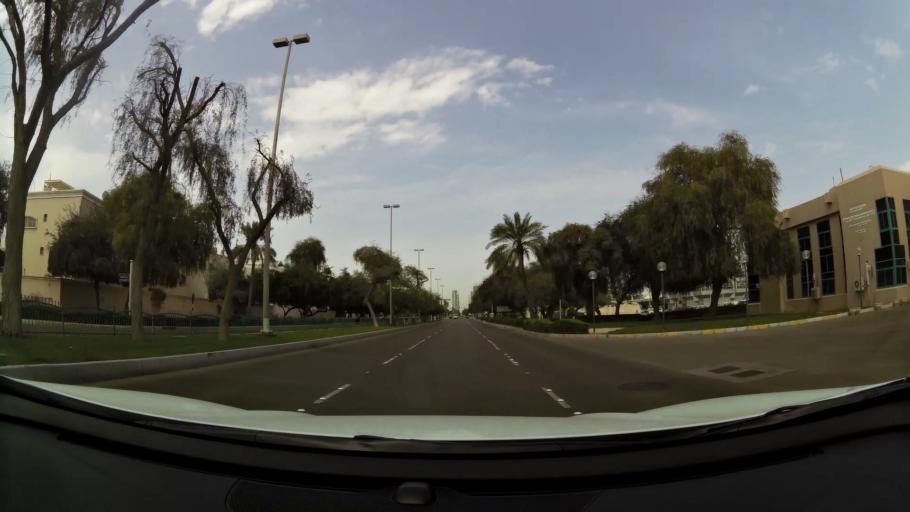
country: AE
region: Abu Dhabi
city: Abu Dhabi
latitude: 24.4582
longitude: 54.3482
